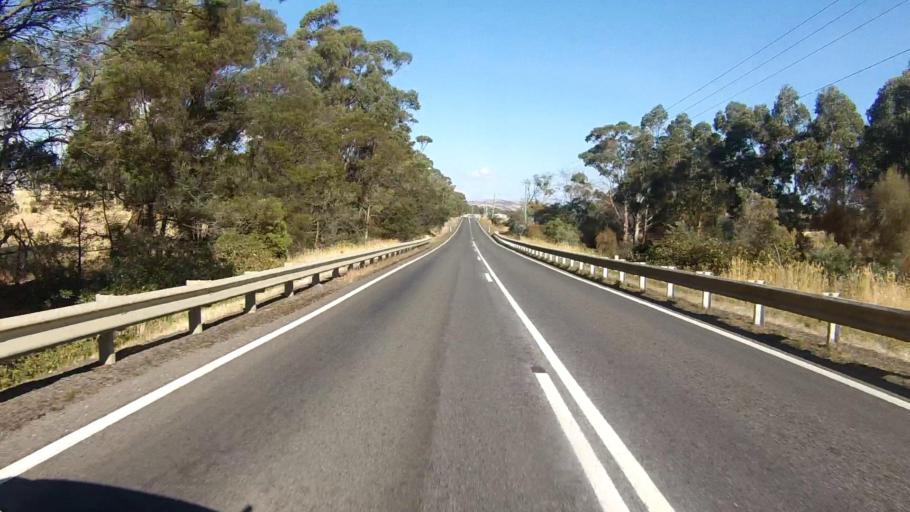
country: AU
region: Tasmania
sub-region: Sorell
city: Sorell
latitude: -42.7138
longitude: 147.5142
